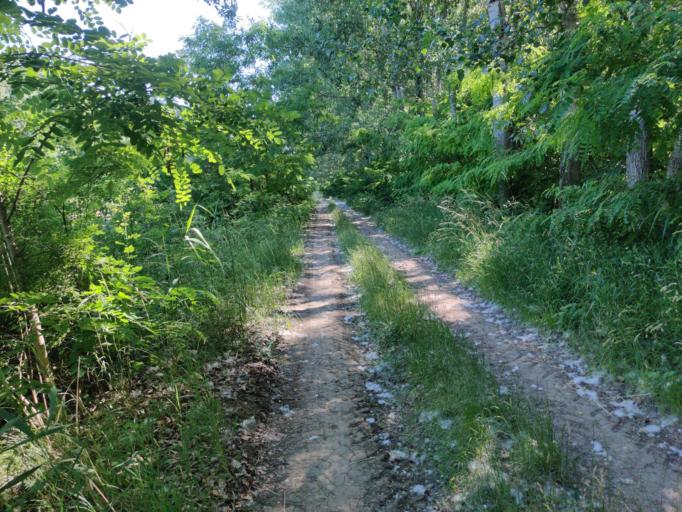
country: HU
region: Hajdu-Bihar
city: Balmazujvaros
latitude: 47.5845
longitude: 21.3562
